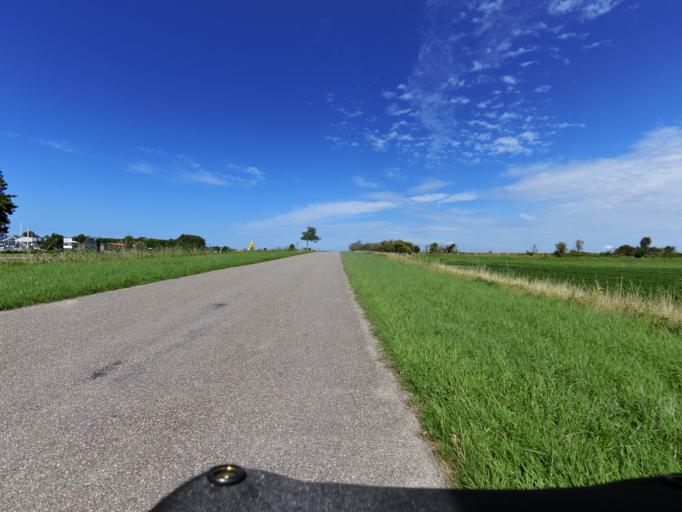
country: NL
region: Zeeland
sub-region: Gemeente Noord-Beveland
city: Kamperland
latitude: 51.5562
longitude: 3.6922
